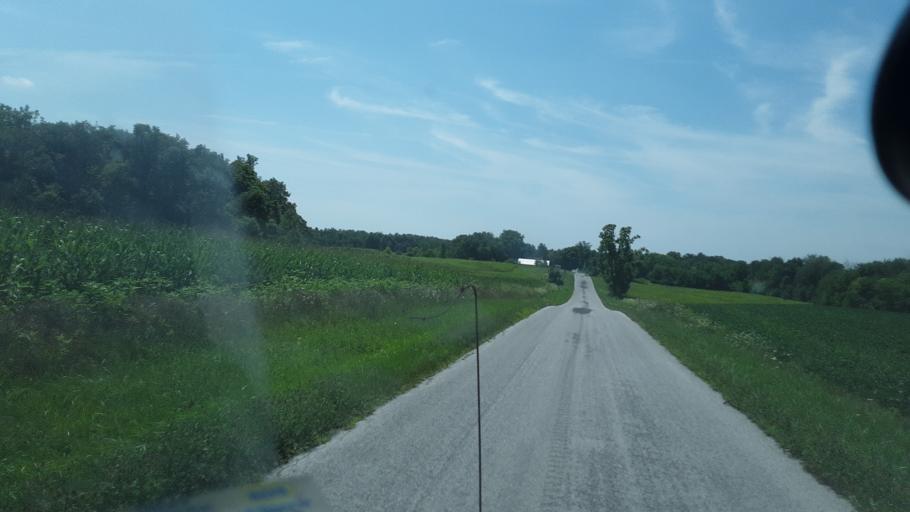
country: US
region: Ohio
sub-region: Hardin County
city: Forest
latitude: 40.7725
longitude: -83.5669
